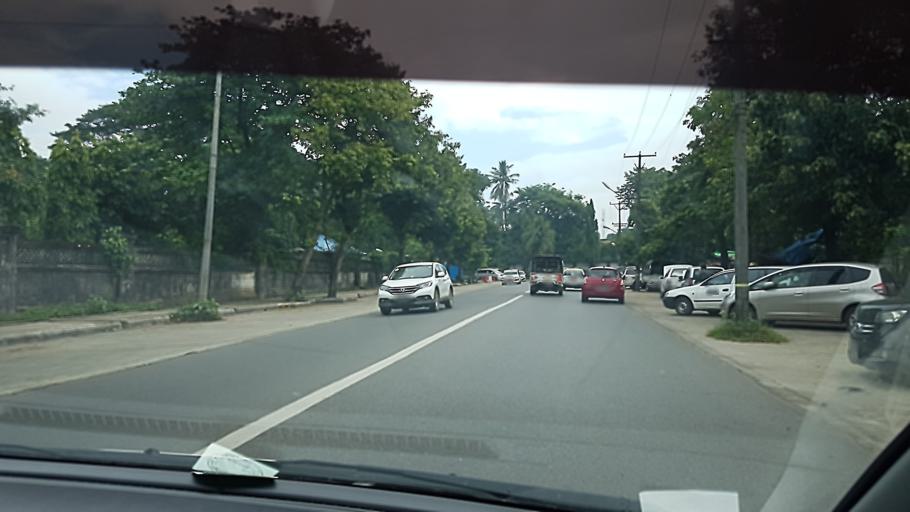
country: MM
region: Yangon
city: Yangon
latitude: 16.7912
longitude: 96.1447
